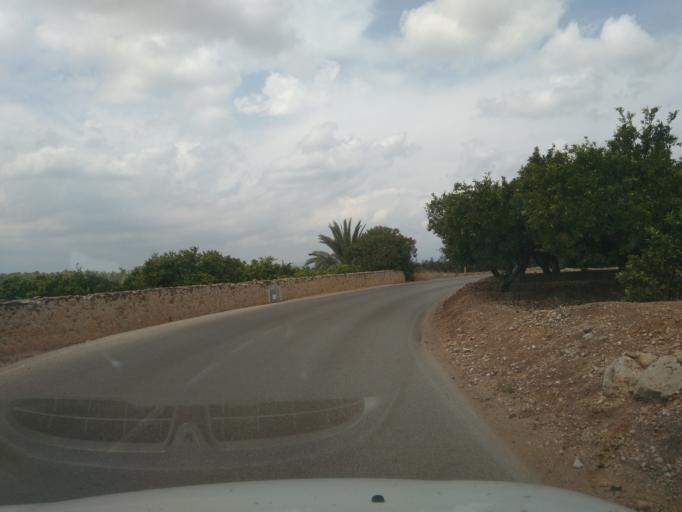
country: ES
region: Valencia
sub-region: Provincia de Valencia
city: La Pobla Llarga
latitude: 39.0898
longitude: -0.4270
